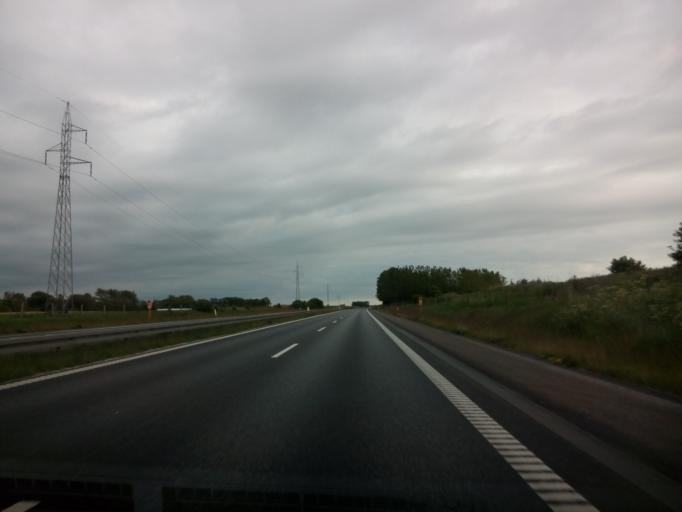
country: DK
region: North Denmark
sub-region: Hjorring Kommune
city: Vra
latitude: 57.3337
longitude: 10.0270
